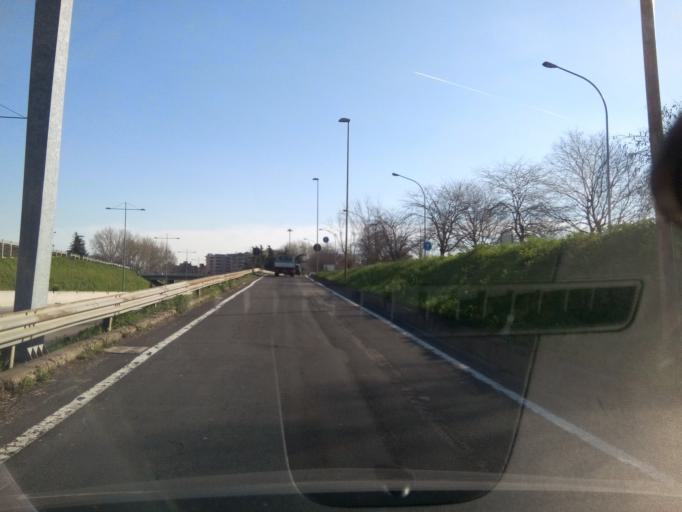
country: IT
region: Emilia-Romagna
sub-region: Provincia di Bologna
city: Casalecchio di Reno
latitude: 44.4986
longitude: 11.3015
